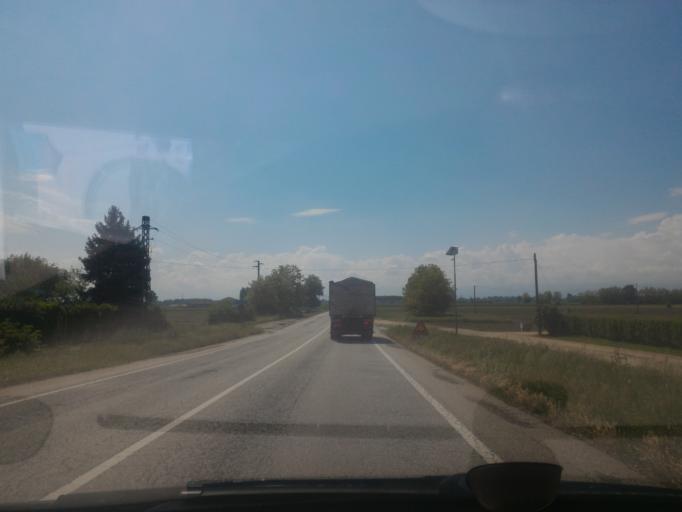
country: IT
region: Piedmont
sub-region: Provincia di Torino
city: Villastellone
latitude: 44.9211
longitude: 7.7270
